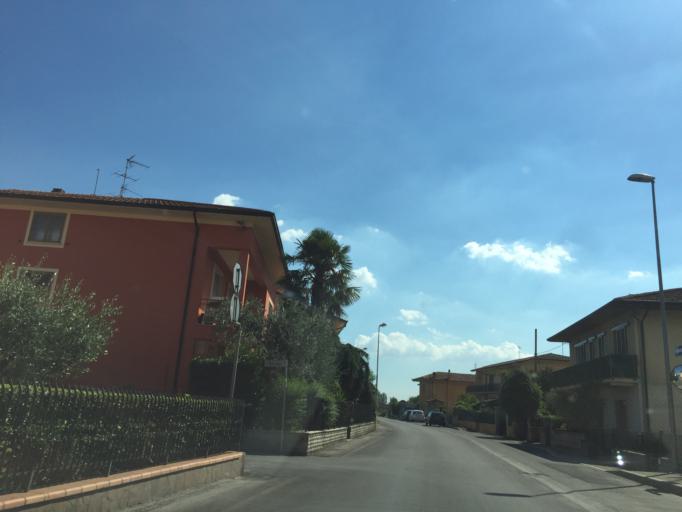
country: IT
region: Tuscany
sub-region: Provincia di Pistoia
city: Monsummano Terme
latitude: 43.8579
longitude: 10.8052
